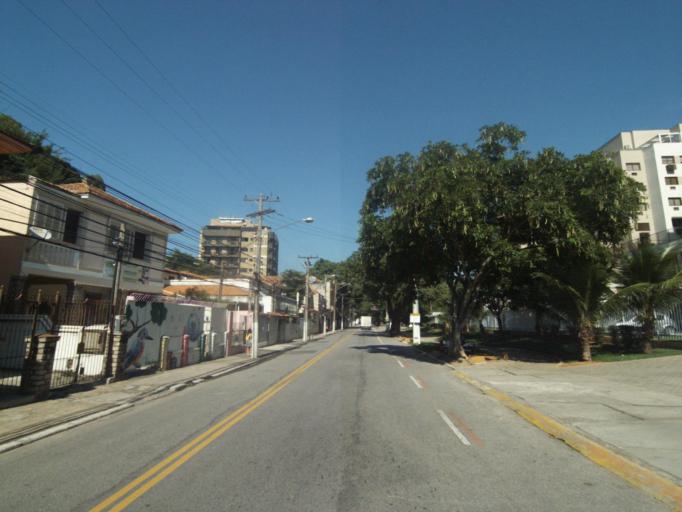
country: BR
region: Rio de Janeiro
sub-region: Niteroi
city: Niteroi
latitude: -22.9012
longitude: -43.1327
